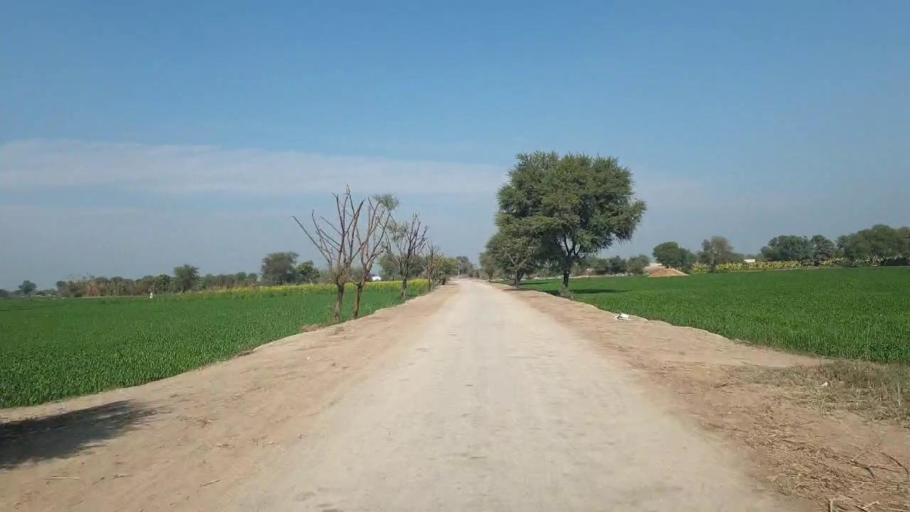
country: PK
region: Sindh
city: Shahdadpur
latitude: 25.9785
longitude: 68.5292
